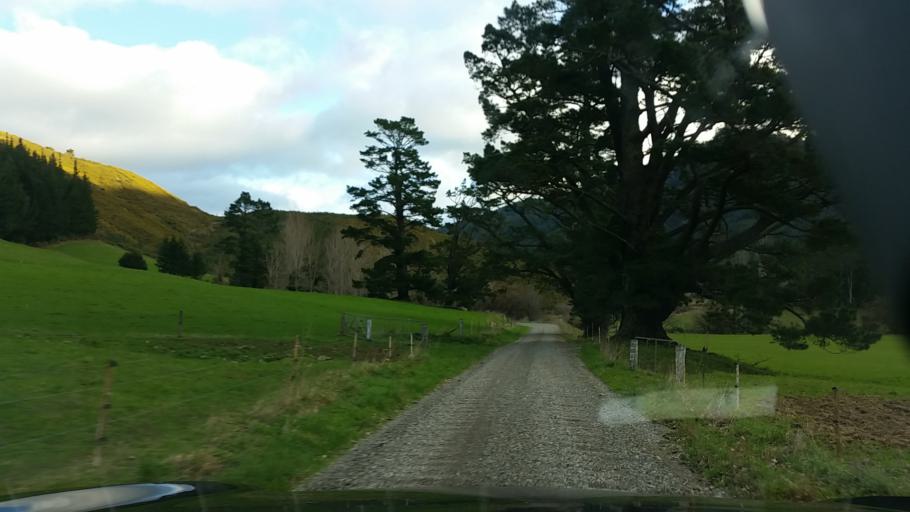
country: NZ
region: Nelson
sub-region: Nelson City
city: Nelson
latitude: -41.1810
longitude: 173.6477
